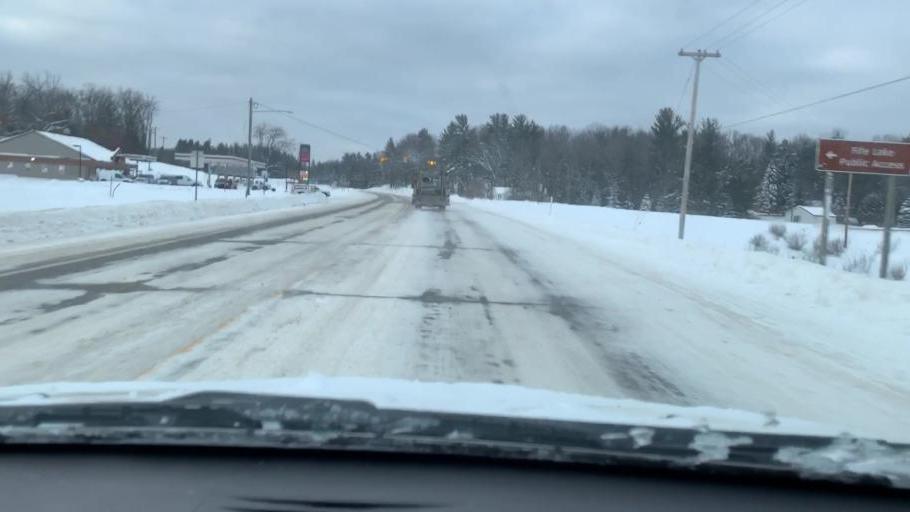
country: US
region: Michigan
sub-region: Wexford County
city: Manton
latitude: 44.5779
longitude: -85.3633
